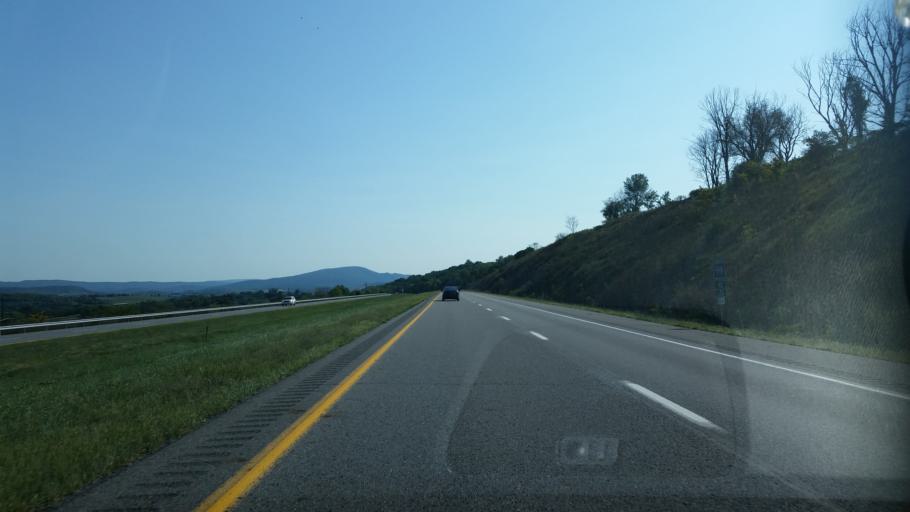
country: US
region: Pennsylvania
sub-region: Bedford County
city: Bedford
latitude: 40.1388
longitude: -78.5144
